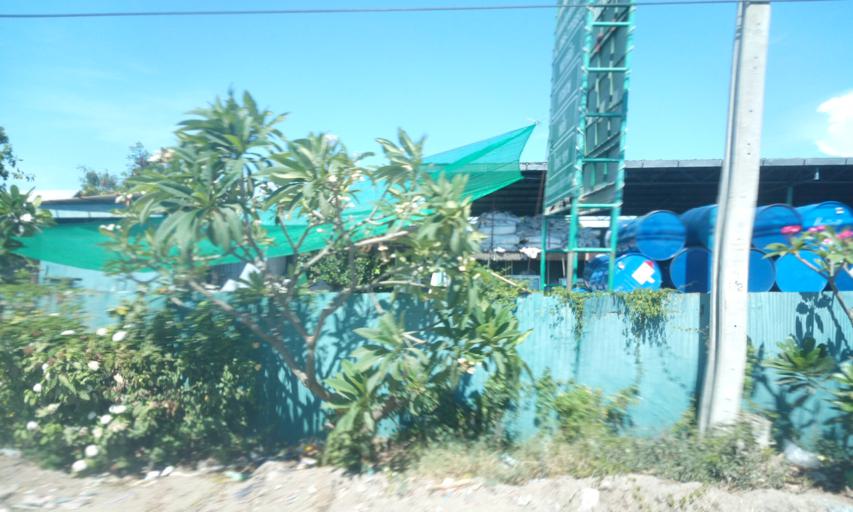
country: TH
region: Samut Prakan
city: Bang Bo District
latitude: 13.5365
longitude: 100.7882
